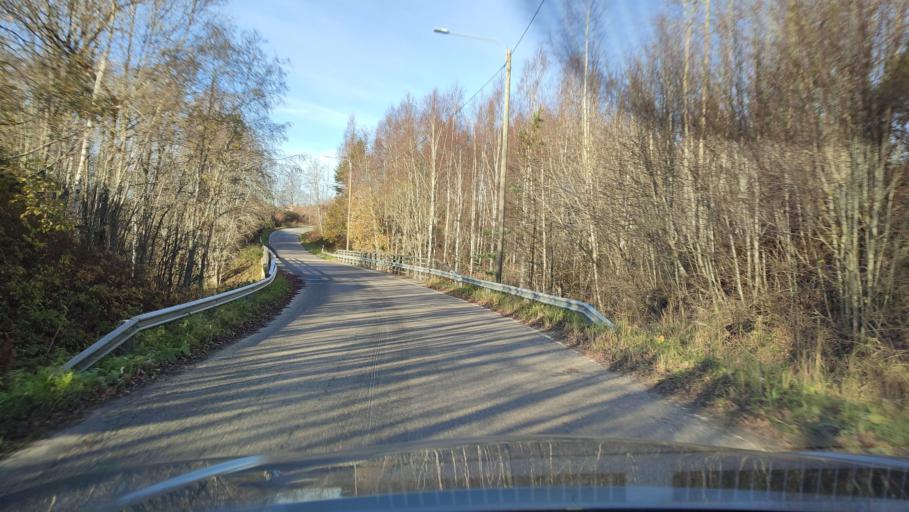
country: FI
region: Southern Ostrobothnia
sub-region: Suupohja
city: Teuva
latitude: 62.4492
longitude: 21.6069
